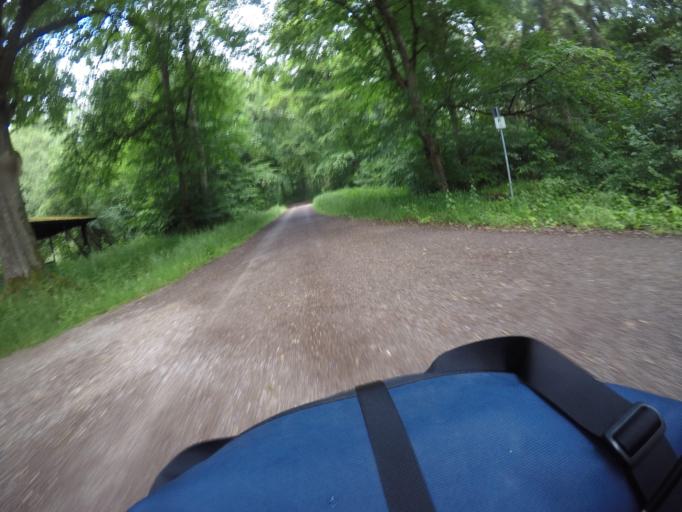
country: DE
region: Baden-Wuerttemberg
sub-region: Regierungsbezirk Stuttgart
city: Gerlingen
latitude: 48.7592
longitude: 9.0867
